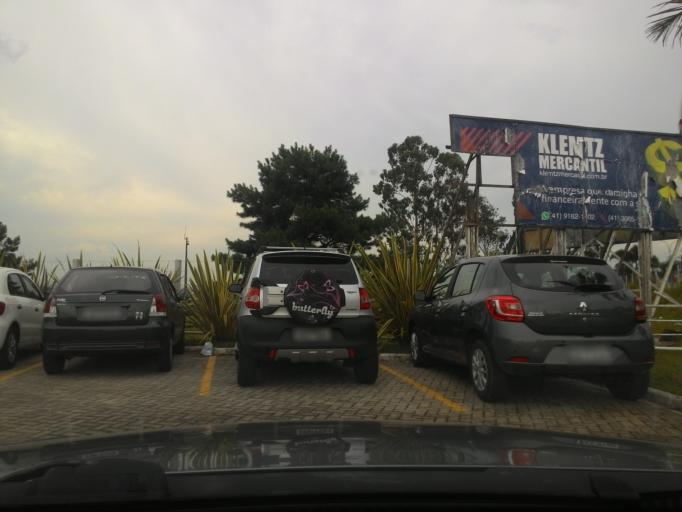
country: BR
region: Parana
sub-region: Pinhais
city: Pinhais
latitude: -25.4367
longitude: -49.1853
